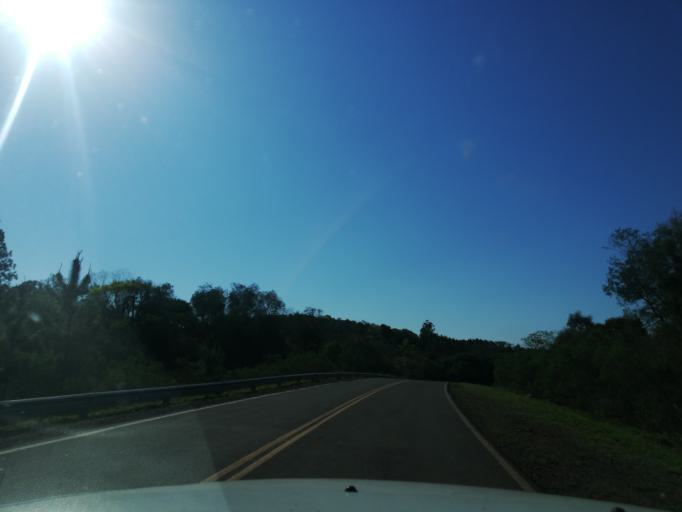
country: AR
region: Misiones
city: Arroyo del Medio
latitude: -27.6828
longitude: -55.3984
